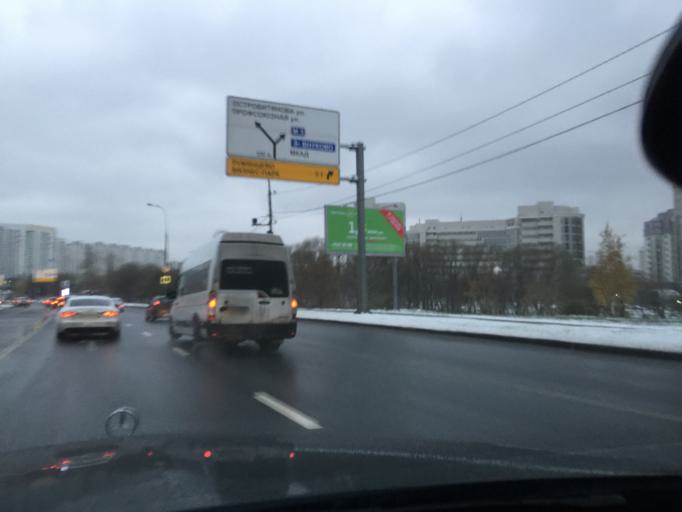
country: RU
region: Moscow
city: Troparevo
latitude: 55.6538
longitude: 37.4796
